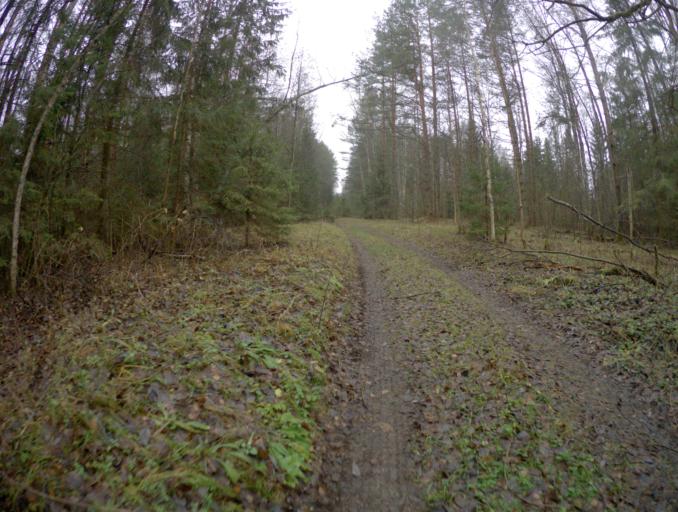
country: RU
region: Vladimir
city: Golovino
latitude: 56.0121
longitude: 40.4829
